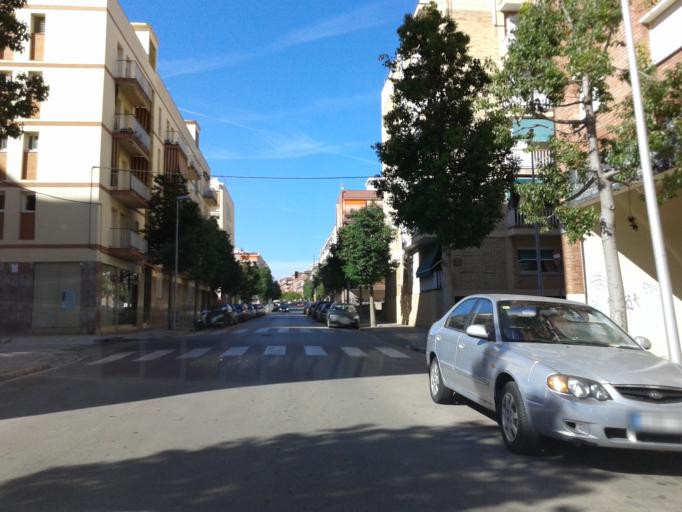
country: ES
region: Catalonia
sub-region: Provincia de Barcelona
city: Vilanova i la Geltru
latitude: 41.2198
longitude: 1.7157
